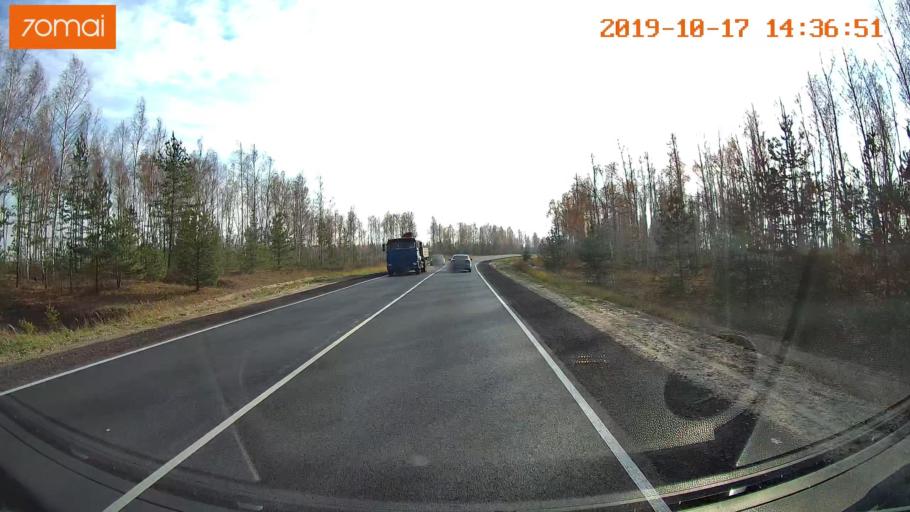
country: RU
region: Rjazan
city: Solotcha
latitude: 54.8860
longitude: 40.0005
